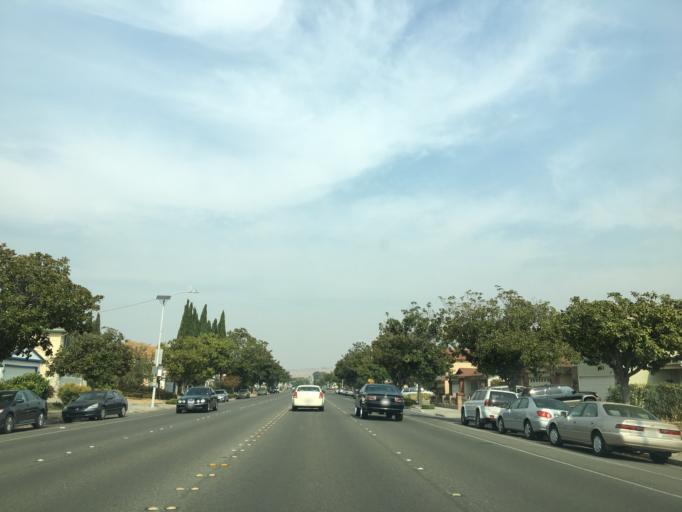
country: US
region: California
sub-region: Santa Clara County
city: Milpitas
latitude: 37.4314
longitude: -121.8828
